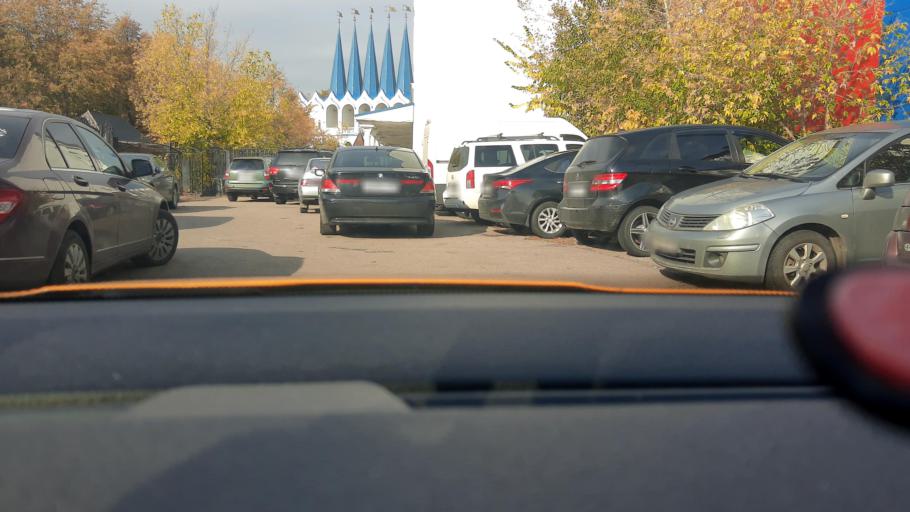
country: RU
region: Moscow
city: Metrogorodok
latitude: 55.7958
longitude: 37.7516
